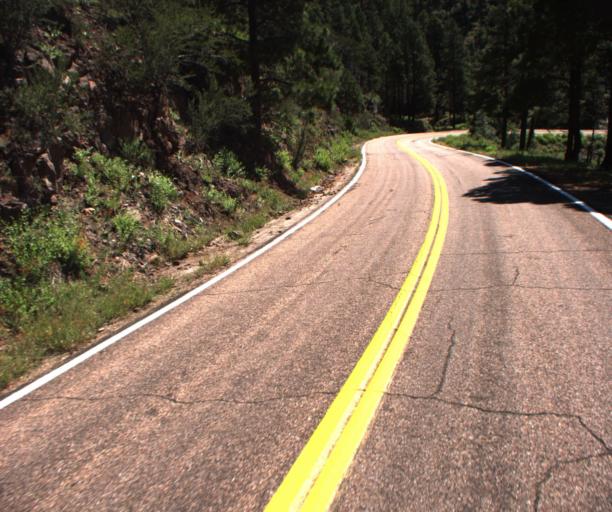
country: US
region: Arizona
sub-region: Greenlee County
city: Morenci
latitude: 33.5592
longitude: -109.3278
